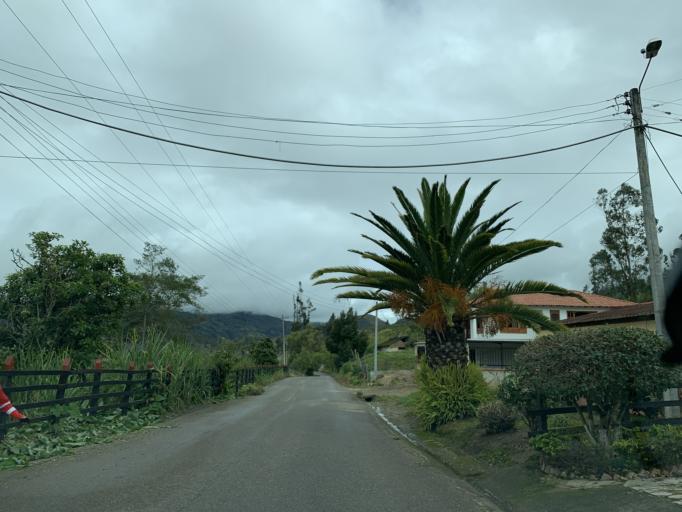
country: CO
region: Boyaca
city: Tibana
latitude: 5.3126
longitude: -73.4079
